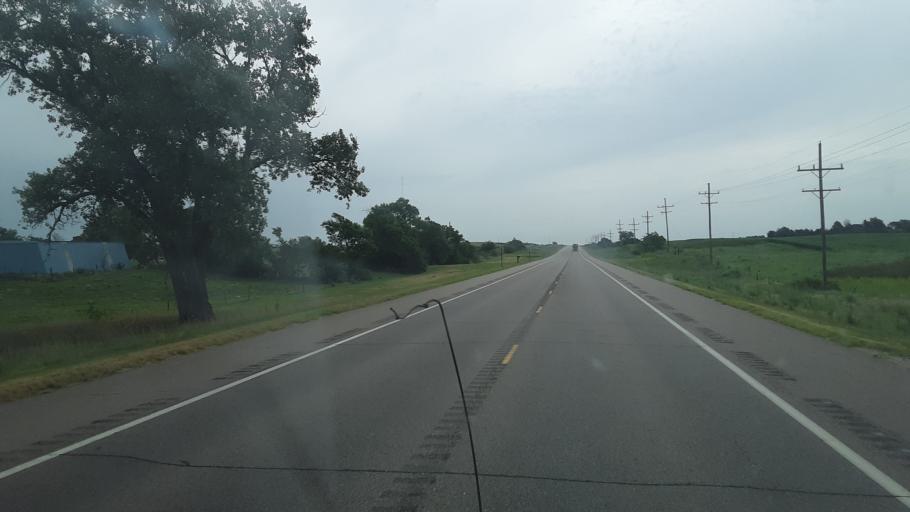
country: US
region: Kansas
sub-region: Edwards County
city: Kinsley
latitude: 37.9275
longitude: -99.3505
